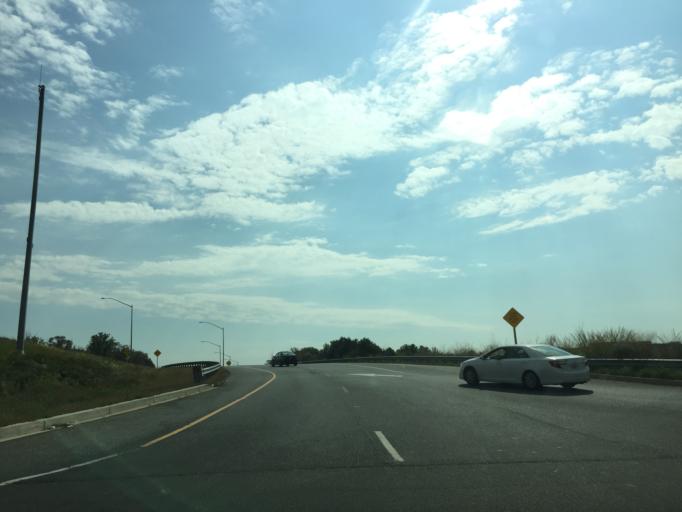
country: US
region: Maryland
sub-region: Harford County
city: Bel Air South
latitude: 39.4644
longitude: -76.3143
